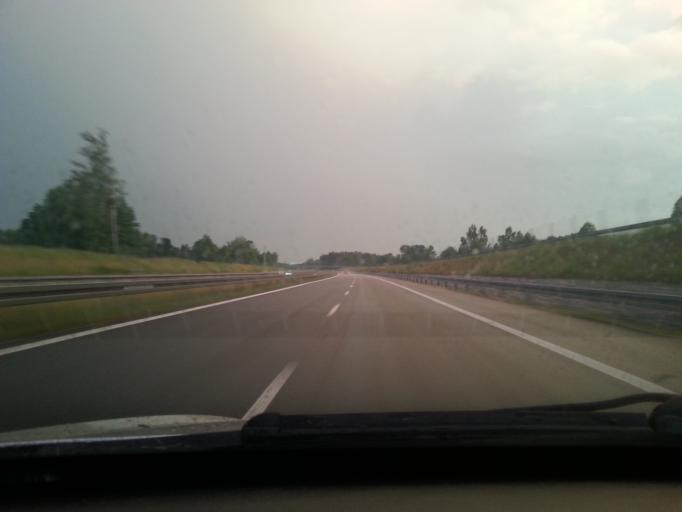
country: PL
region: Lodz Voivodeship
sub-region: Powiat pabianicki
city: Dobron
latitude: 51.6595
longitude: 19.2752
